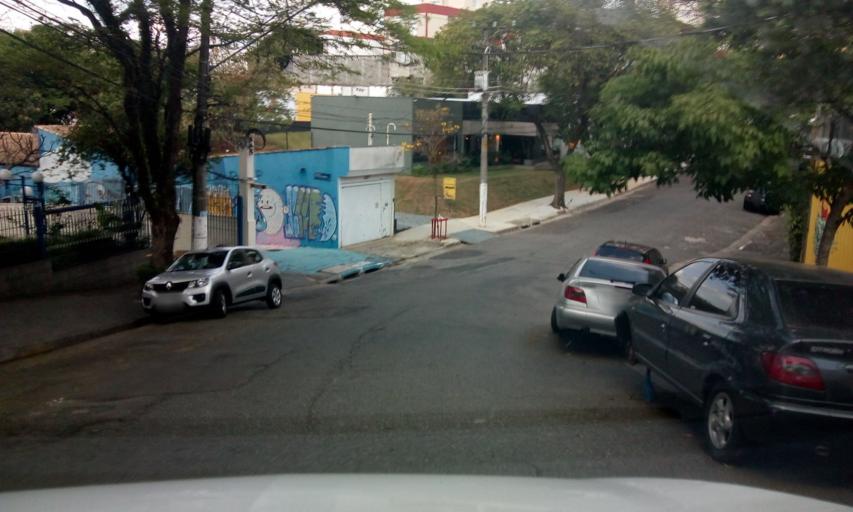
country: BR
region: Sao Paulo
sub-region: Sao Paulo
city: Sao Paulo
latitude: -23.5340
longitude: -46.7037
